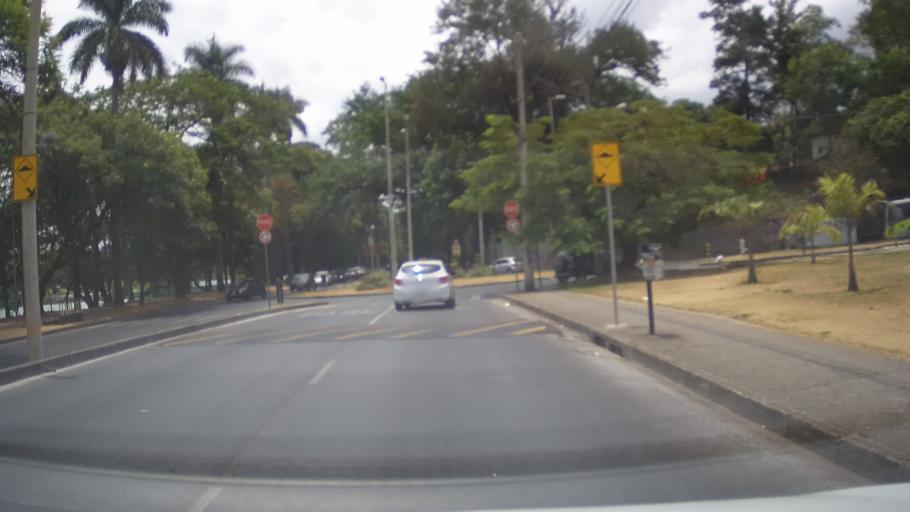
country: BR
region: Minas Gerais
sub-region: Belo Horizonte
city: Belo Horizonte
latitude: -19.8613
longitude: -43.9747
